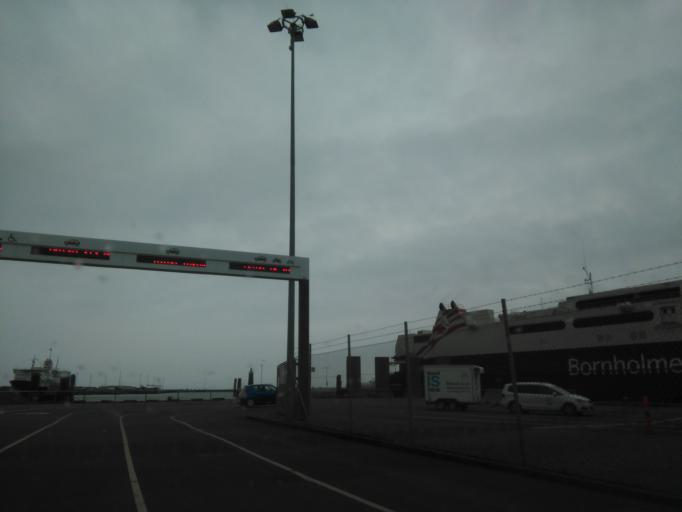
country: DK
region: Capital Region
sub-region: Bornholm Kommune
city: Ronne
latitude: 55.0996
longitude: 14.6927
